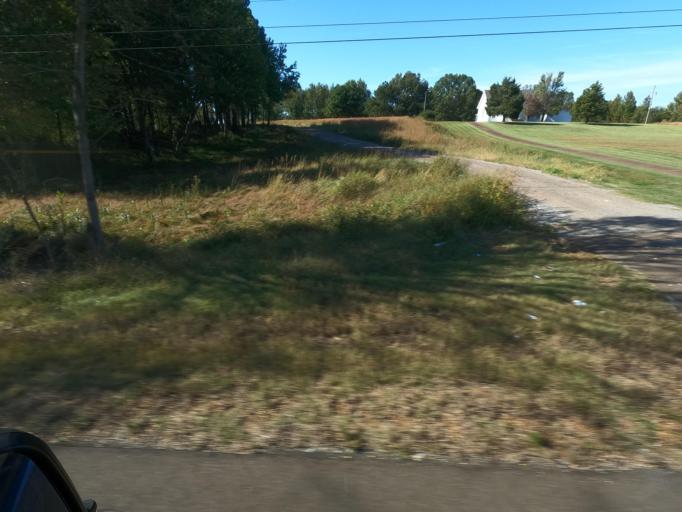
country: US
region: Tennessee
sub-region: Obion County
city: Englewood
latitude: 36.3780
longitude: -89.1150
